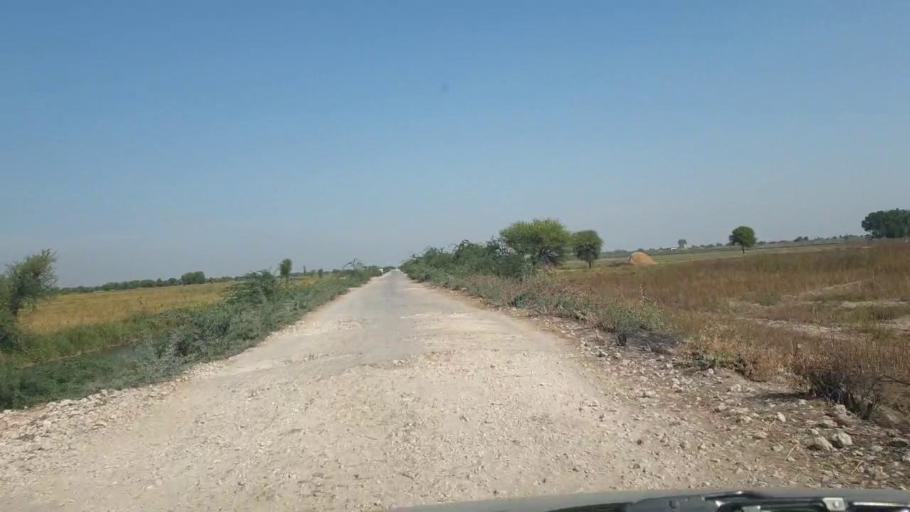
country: PK
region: Sindh
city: Tando Bago
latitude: 24.8230
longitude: 68.9862
